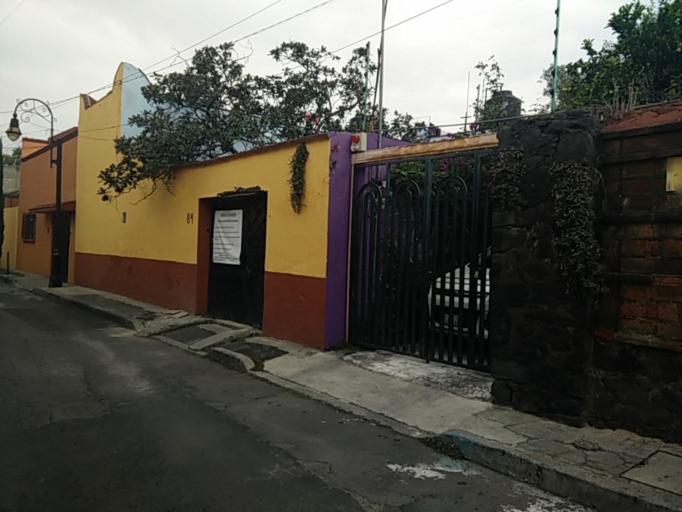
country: MX
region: Mexico City
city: Coyoacan
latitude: 19.3451
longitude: -99.1607
